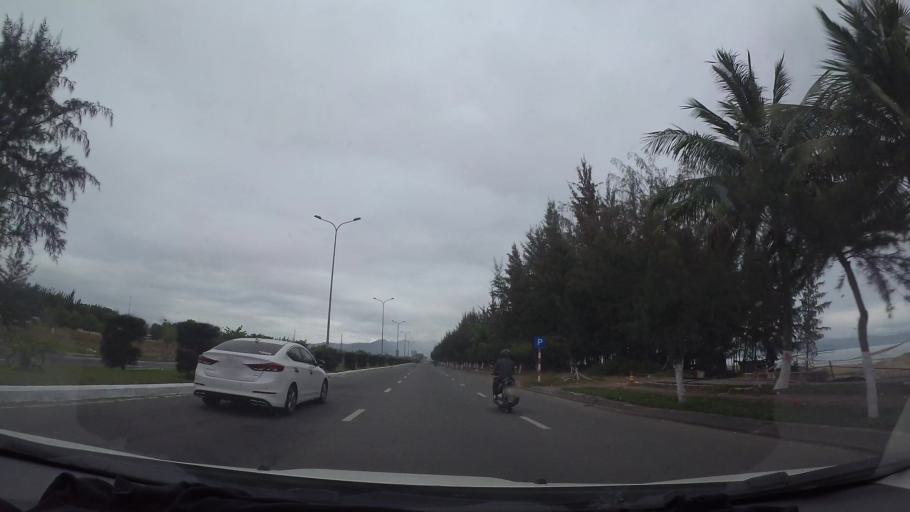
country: VN
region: Da Nang
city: Lien Chieu
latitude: 16.0964
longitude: 108.1449
